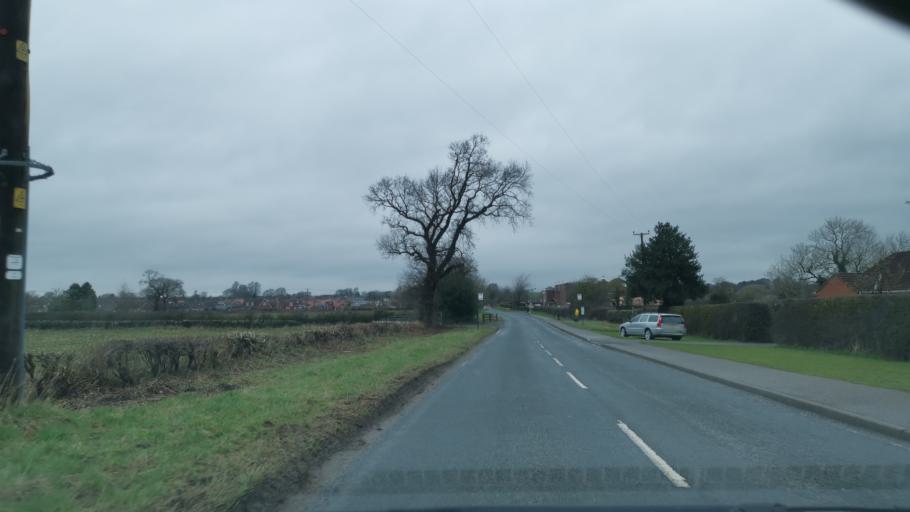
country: GB
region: England
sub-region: City of York
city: Holtby
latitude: 53.9595
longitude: -0.9741
